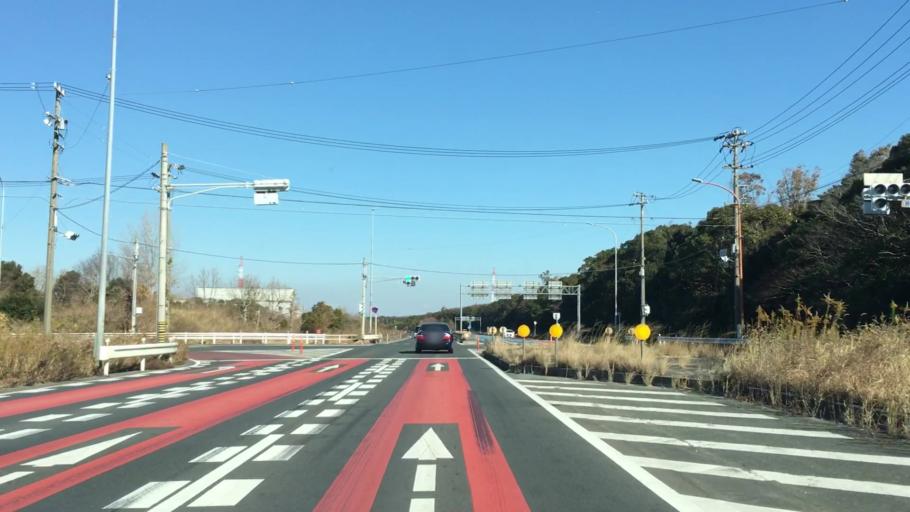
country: JP
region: Aichi
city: Tahara
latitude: 34.7067
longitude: 137.3316
